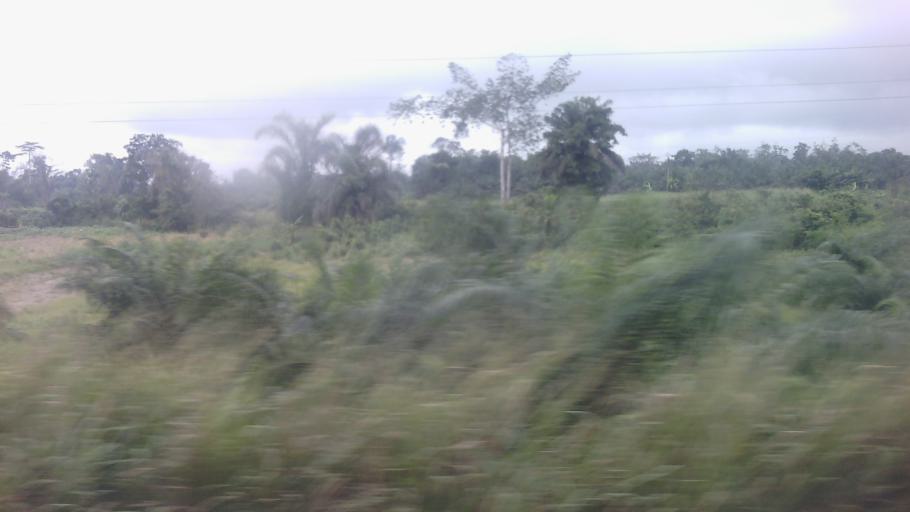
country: CI
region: Sud-Comoe
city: Aboisso
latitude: 5.4143
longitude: -3.2834
